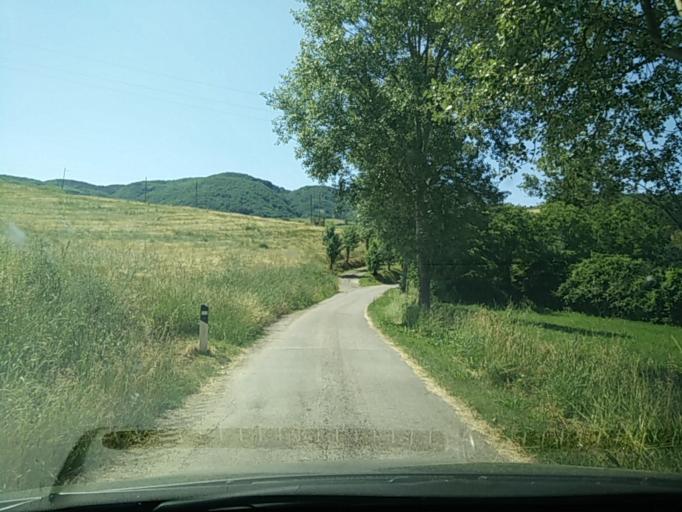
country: IT
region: Lombardy
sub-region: Provincia di Pavia
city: Susella
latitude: 44.8993
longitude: 9.1044
